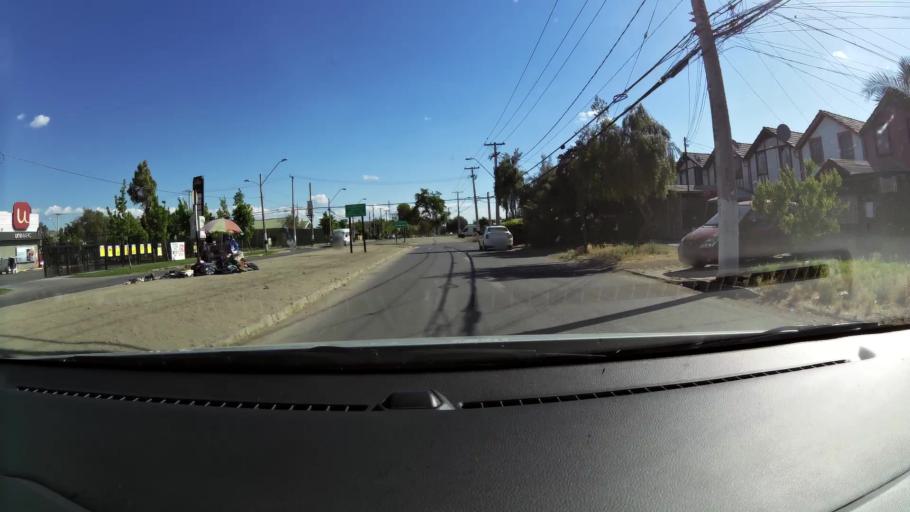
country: CL
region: Santiago Metropolitan
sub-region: Provincia de Maipo
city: San Bernardo
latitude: -33.5415
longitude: -70.7715
